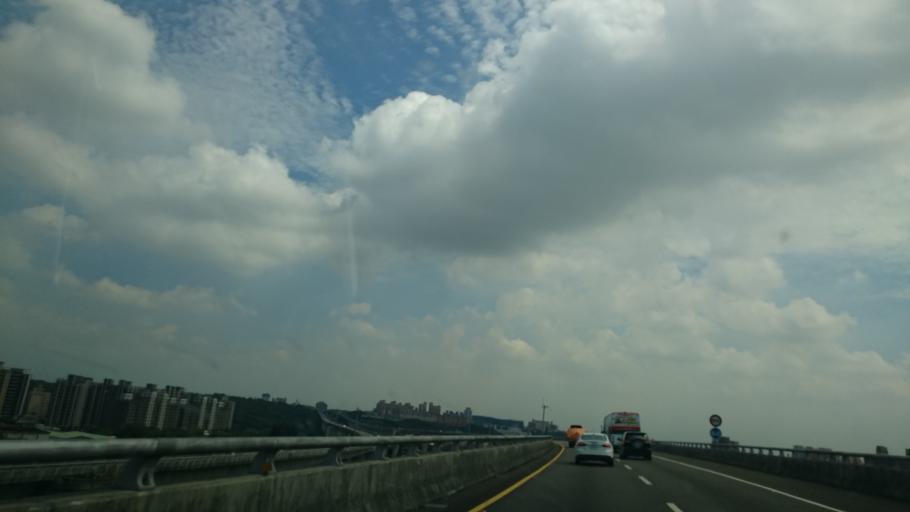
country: TW
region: Taiwan
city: Daxi
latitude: 24.9047
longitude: 121.1621
